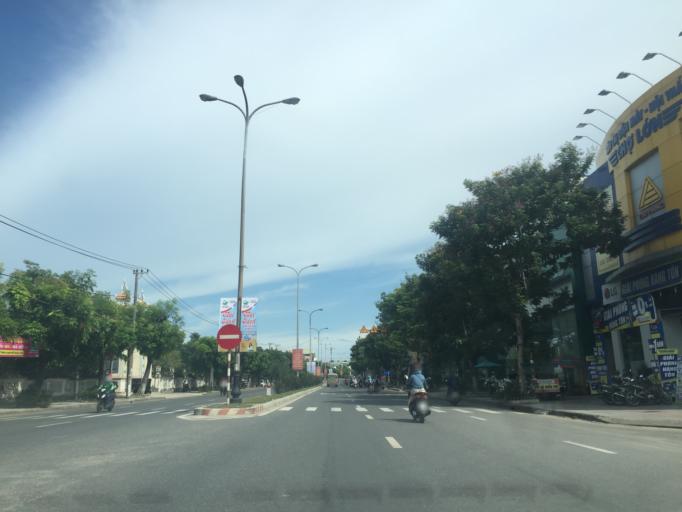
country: VN
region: Da Nang
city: Lien Chieu
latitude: 16.0599
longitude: 108.1632
